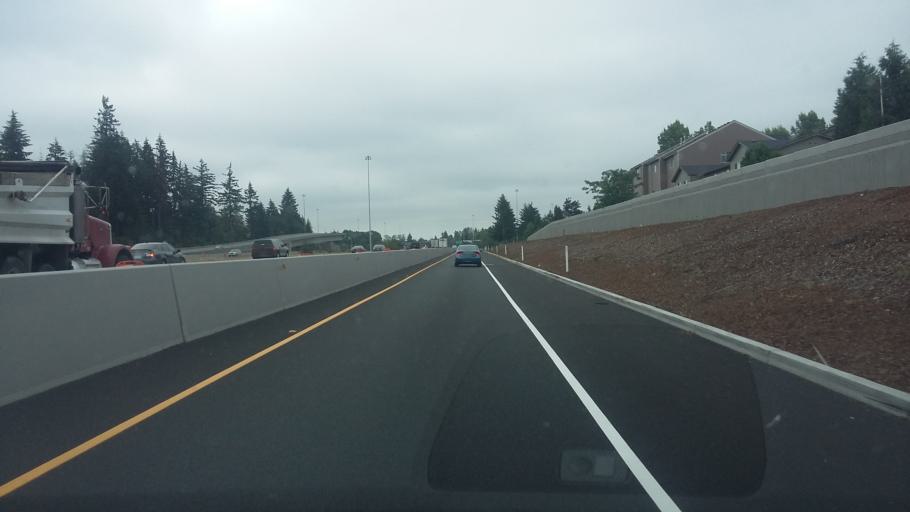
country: US
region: Washington
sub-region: Clark County
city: Orchards
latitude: 45.6279
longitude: -122.5600
